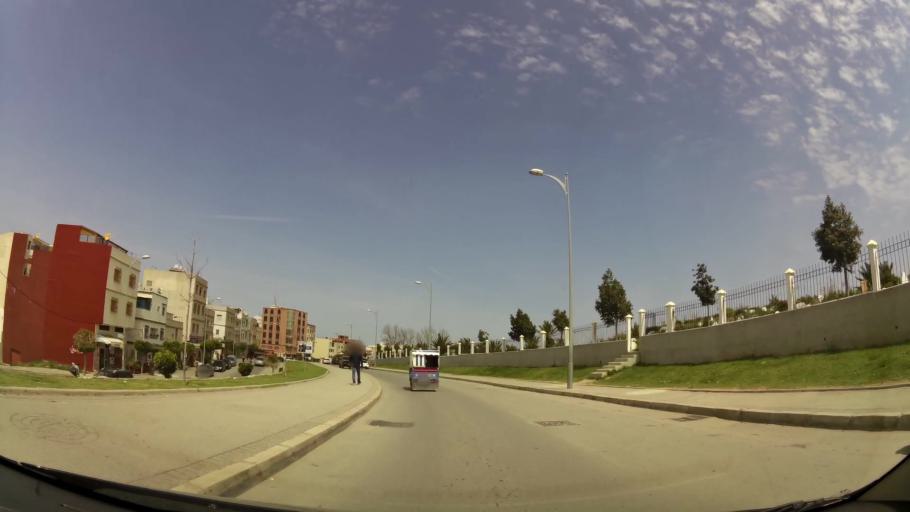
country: MA
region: Tanger-Tetouan
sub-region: Tanger-Assilah
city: Tangier
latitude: 35.7501
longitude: -5.8275
